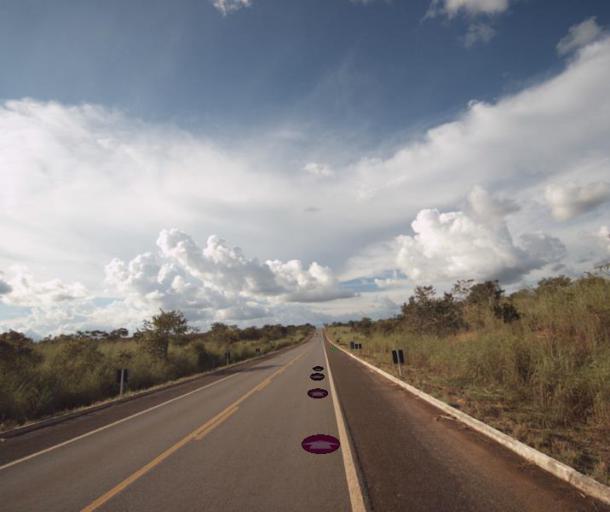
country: BR
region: Goias
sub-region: Barro Alto
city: Barro Alto
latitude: -14.8476
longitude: -48.6387
